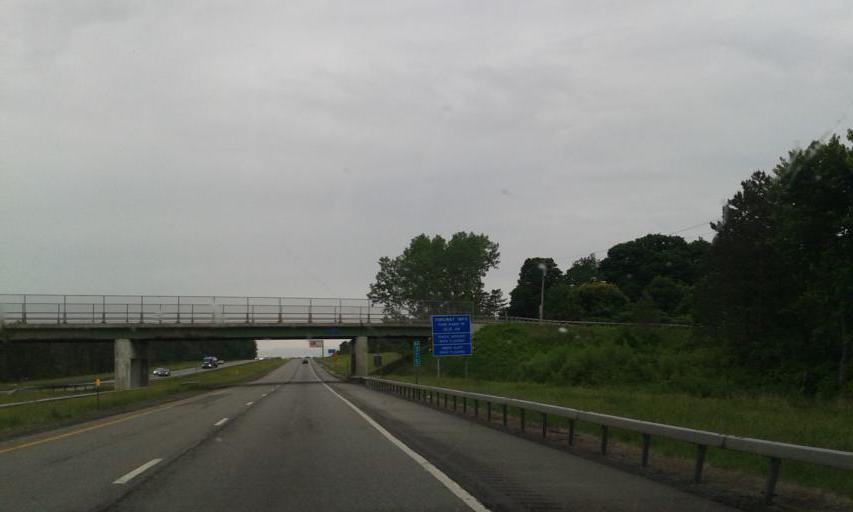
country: US
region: New York
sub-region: Livingston County
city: Caledonia
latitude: 43.0302
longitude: -77.8938
